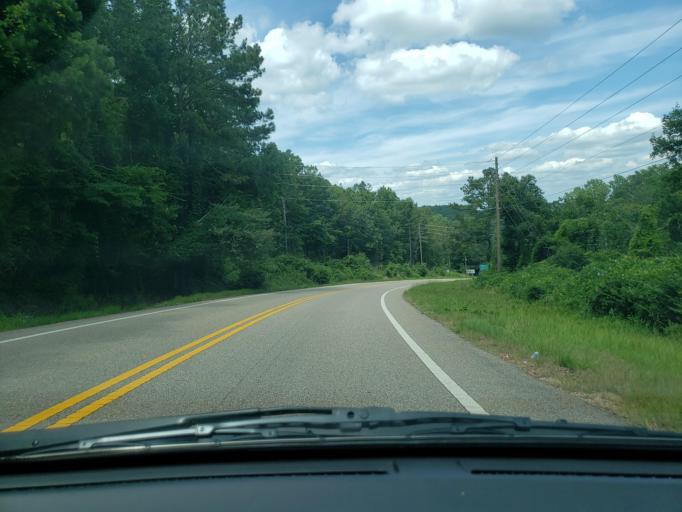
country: US
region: Alabama
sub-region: Elmore County
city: Eclectic
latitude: 32.6734
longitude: -85.9133
